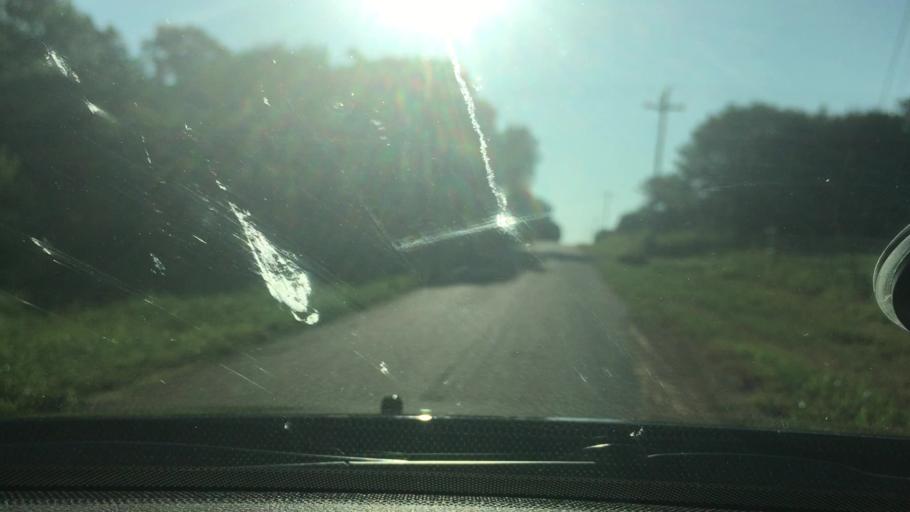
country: US
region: Oklahoma
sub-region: Murray County
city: Sulphur
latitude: 34.4048
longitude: -96.8118
